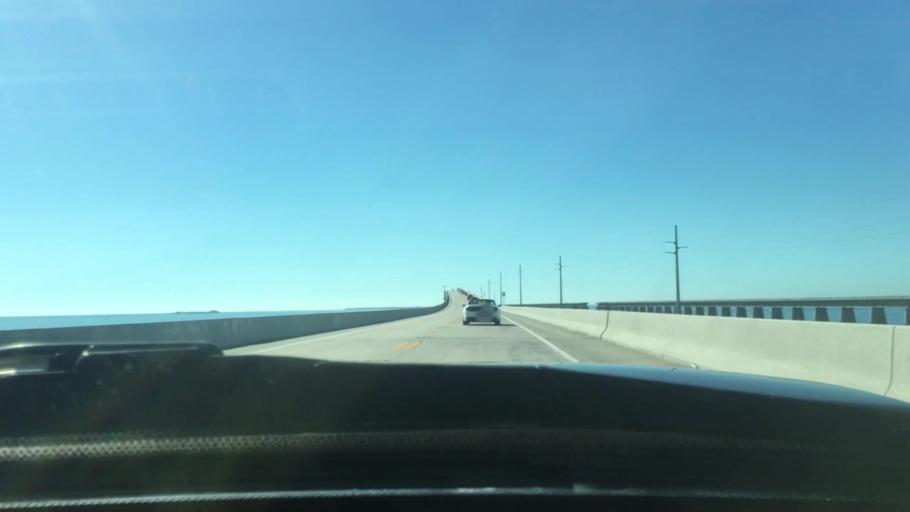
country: US
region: Florida
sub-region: Monroe County
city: Marathon
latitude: 24.7015
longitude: -81.1607
